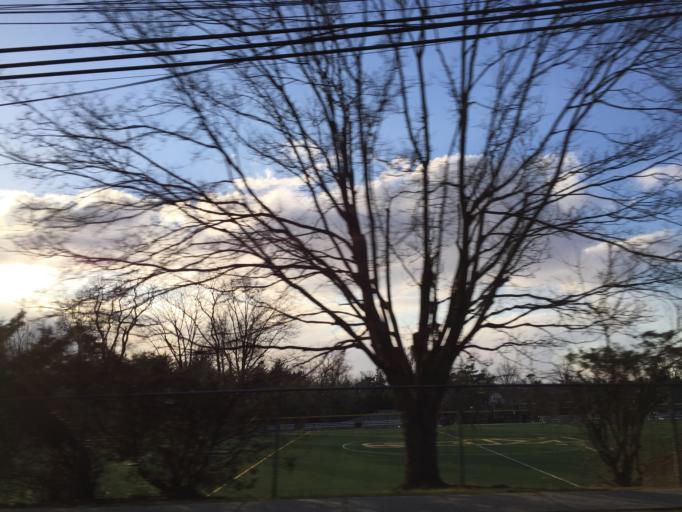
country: US
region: New Jersey
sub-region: Union County
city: Summit
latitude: 40.7189
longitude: -74.3626
